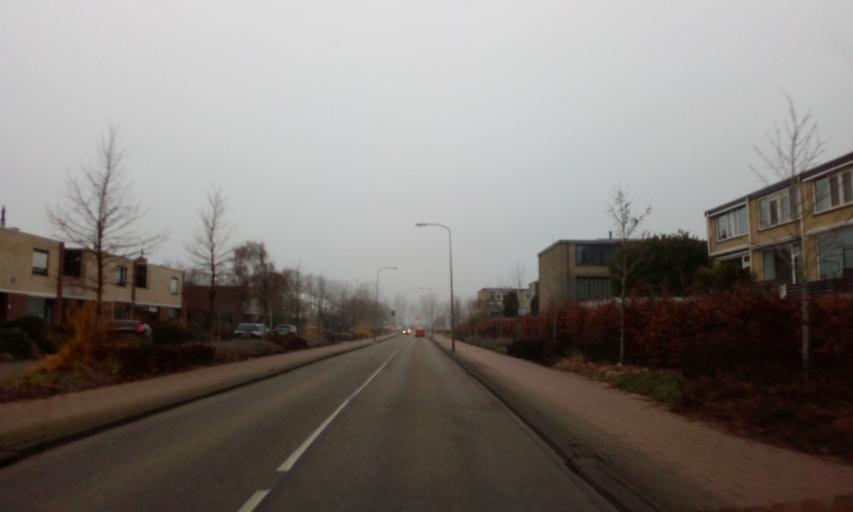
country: NL
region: South Holland
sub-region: Gemeente Capelle aan den IJssel
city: Capelle aan den IJssel
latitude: 51.9643
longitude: 4.6026
